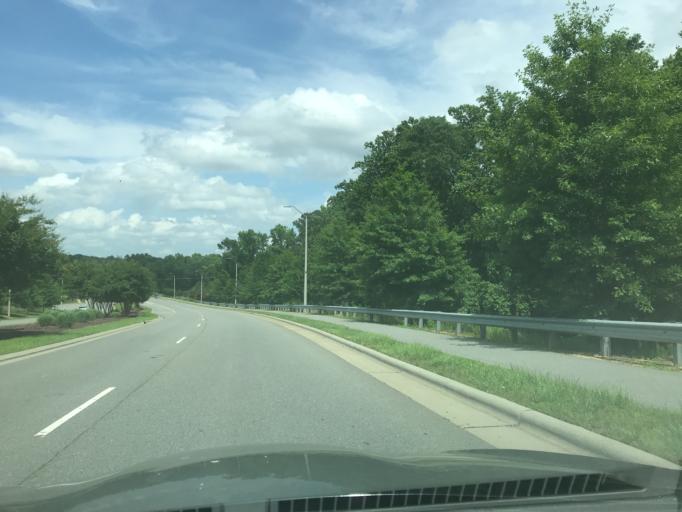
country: US
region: North Carolina
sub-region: Wake County
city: Wake Forest
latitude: 35.9350
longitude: -78.5759
